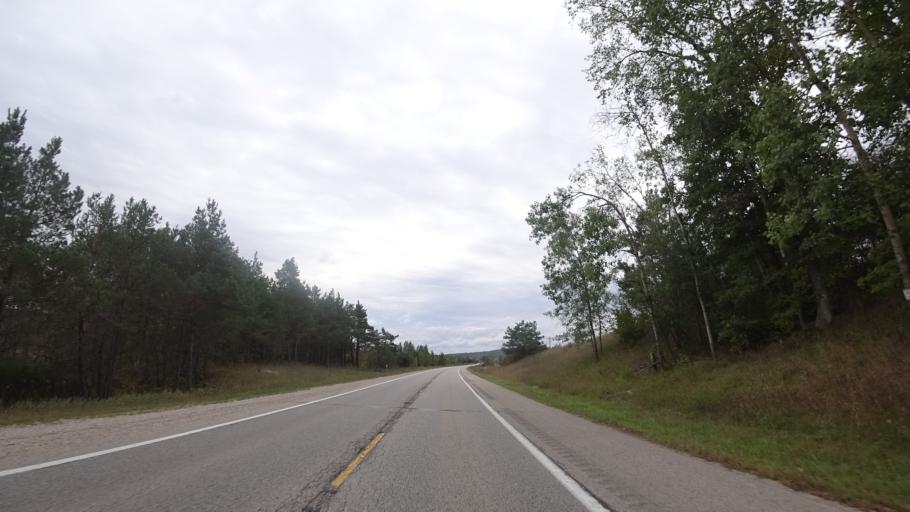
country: US
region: Michigan
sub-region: Charlevoix County
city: Boyne City
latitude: 45.2321
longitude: -84.9170
